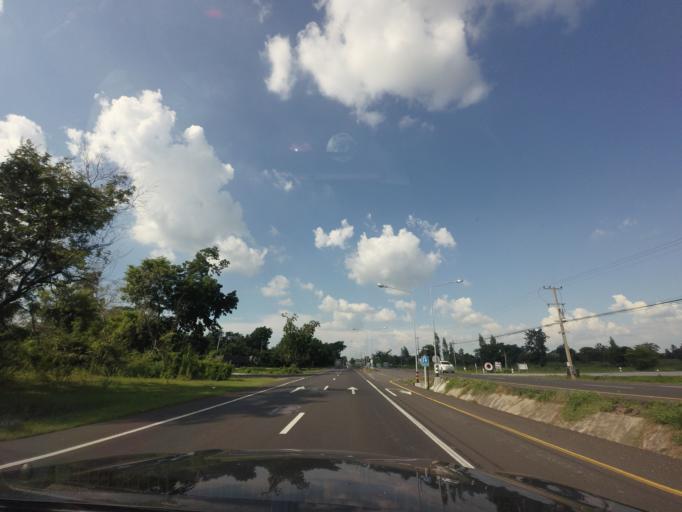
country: TH
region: Nakhon Ratchasima
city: Bua Lai
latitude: 15.7035
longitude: 102.5851
